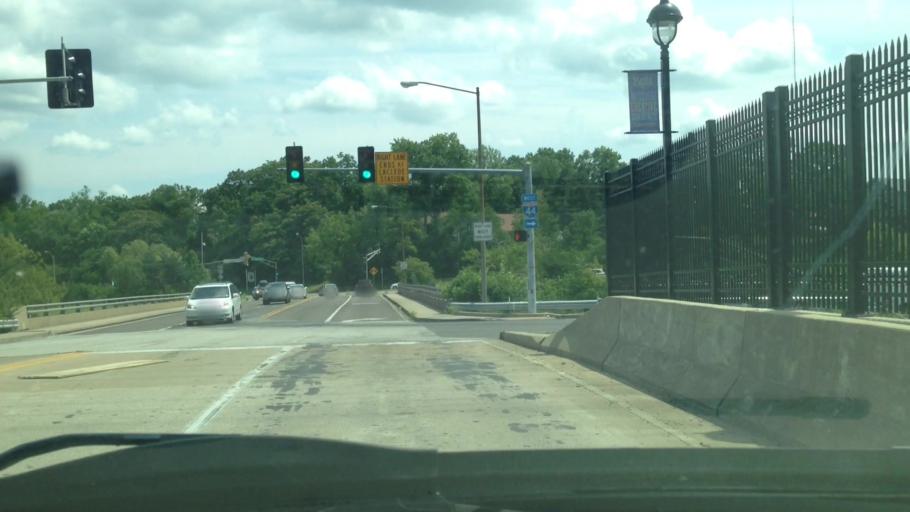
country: US
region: Missouri
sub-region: Saint Louis County
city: Shrewsbury
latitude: 38.5920
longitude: -90.3361
